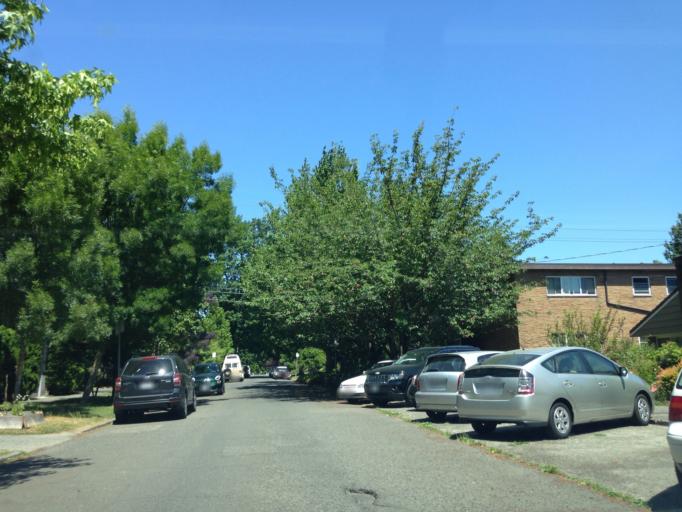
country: US
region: Washington
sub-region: King County
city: Seattle
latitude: 47.6240
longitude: -122.3100
